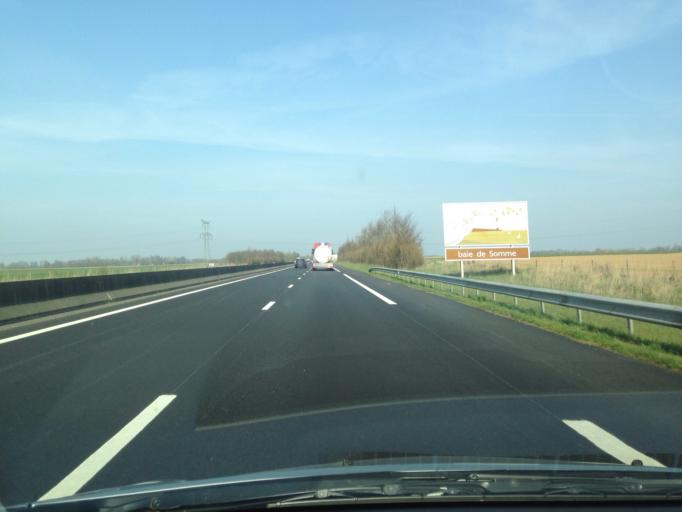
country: FR
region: Picardie
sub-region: Departement de la Somme
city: Oisemont
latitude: 50.0243
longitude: 1.7312
